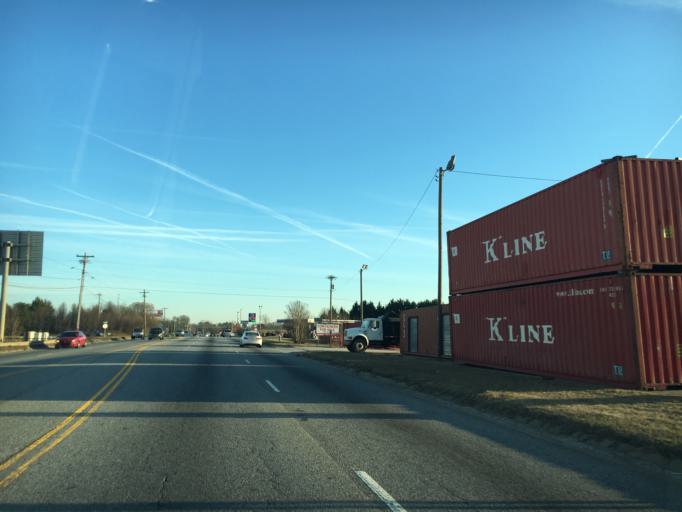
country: US
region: South Carolina
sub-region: Spartanburg County
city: Duncan
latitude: 34.8889
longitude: -82.1562
